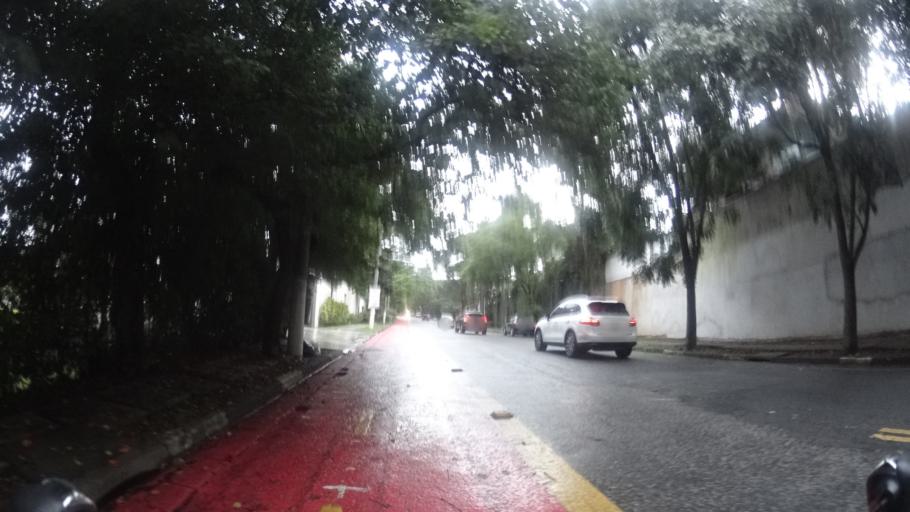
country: BR
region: Sao Paulo
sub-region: Sao Paulo
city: Sao Paulo
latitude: -23.5815
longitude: -46.7040
